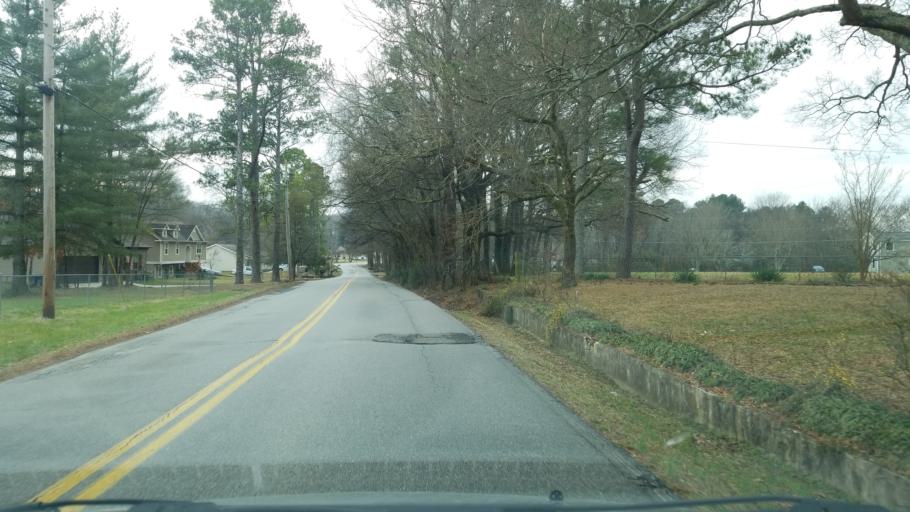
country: US
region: Tennessee
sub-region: Hamilton County
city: East Brainerd
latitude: 34.9878
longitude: -85.1481
